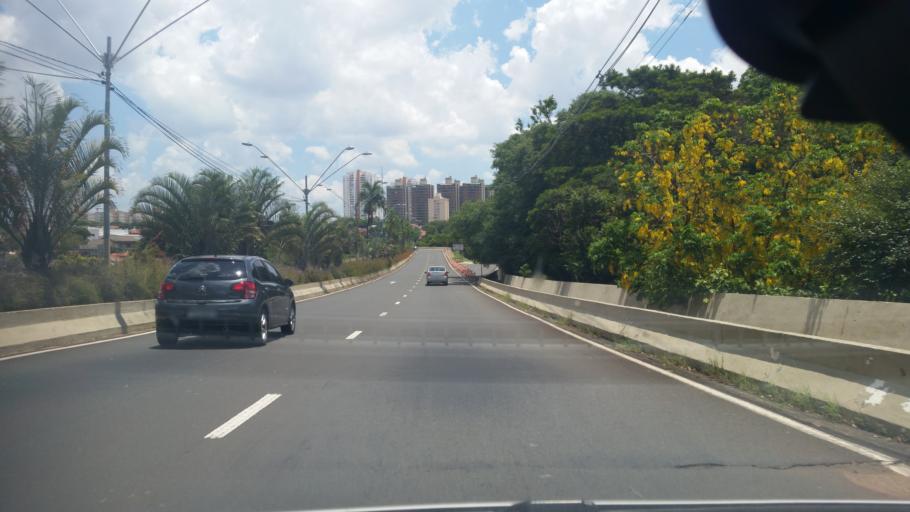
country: BR
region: Sao Paulo
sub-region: Campinas
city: Campinas
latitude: -22.8728
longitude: -47.0456
